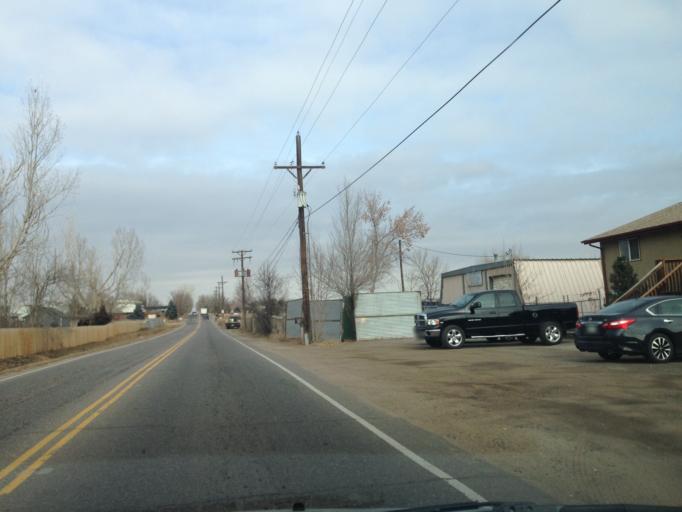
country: US
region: Colorado
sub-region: Boulder County
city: Lafayette
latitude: 39.9870
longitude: -105.0718
